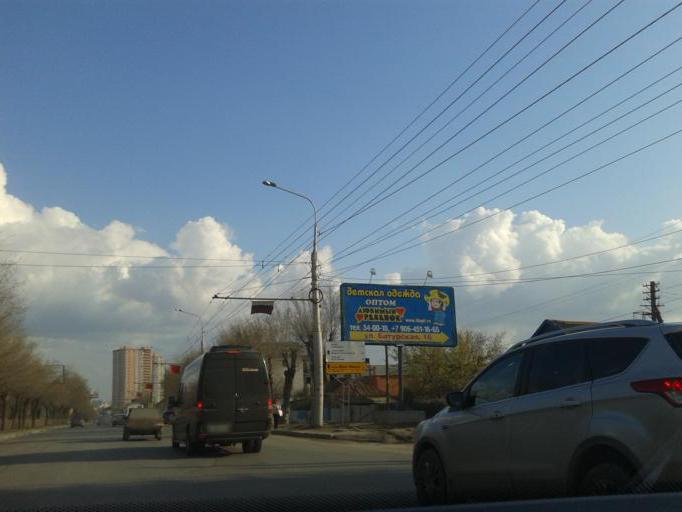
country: RU
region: Volgograd
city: Volgograd
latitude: 48.7281
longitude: 44.4990
